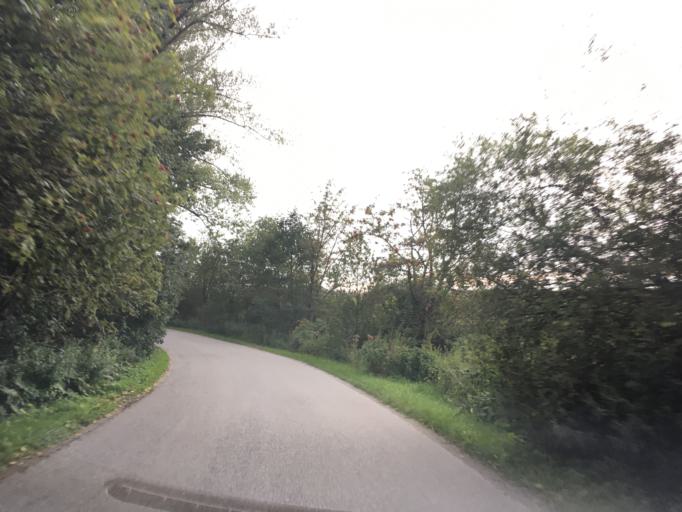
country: SK
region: Zilinsky
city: Namestovo
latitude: 49.4119
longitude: 19.4937
